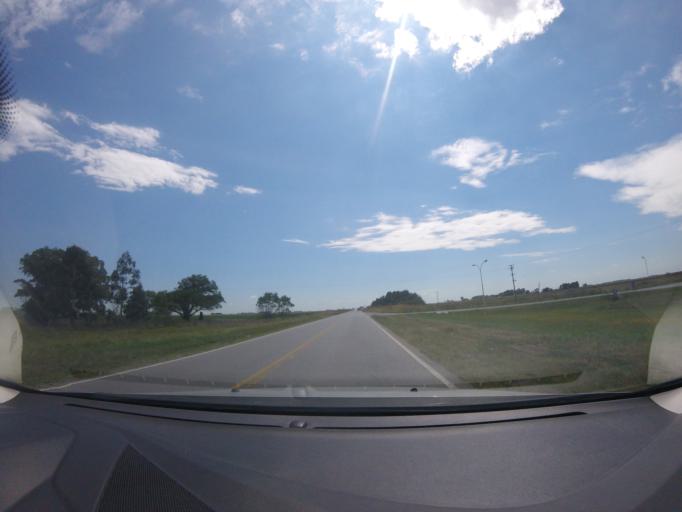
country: AR
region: Buenos Aires
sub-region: Partido de Tandil
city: Tandil
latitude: -37.1799
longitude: -59.0419
